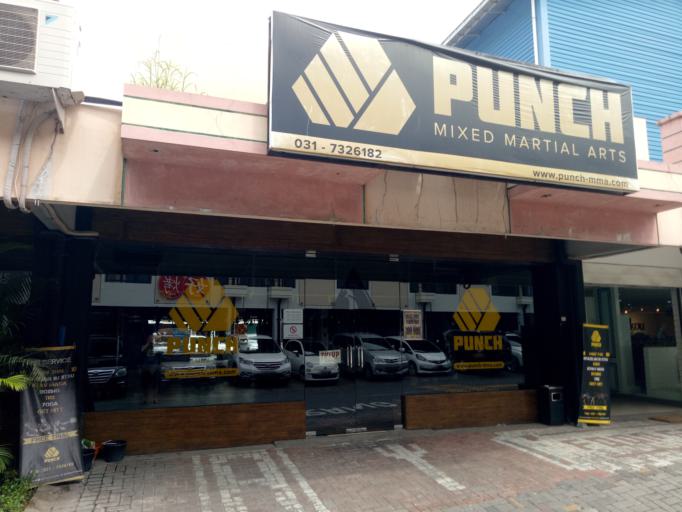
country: ID
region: East Java
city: Jagirsidosermo
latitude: -7.2928
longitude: 112.6767
